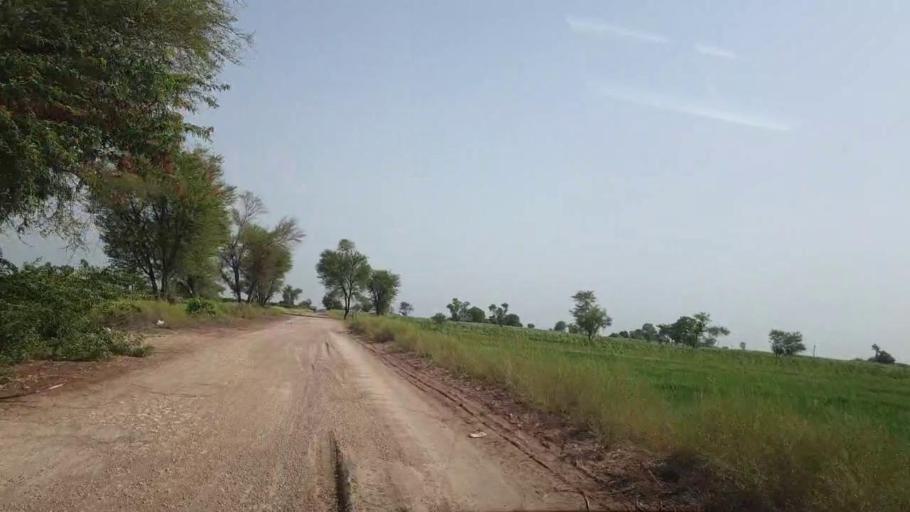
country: PK
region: Sindh
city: Sakrand
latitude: 26.2933
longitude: 68.2214
